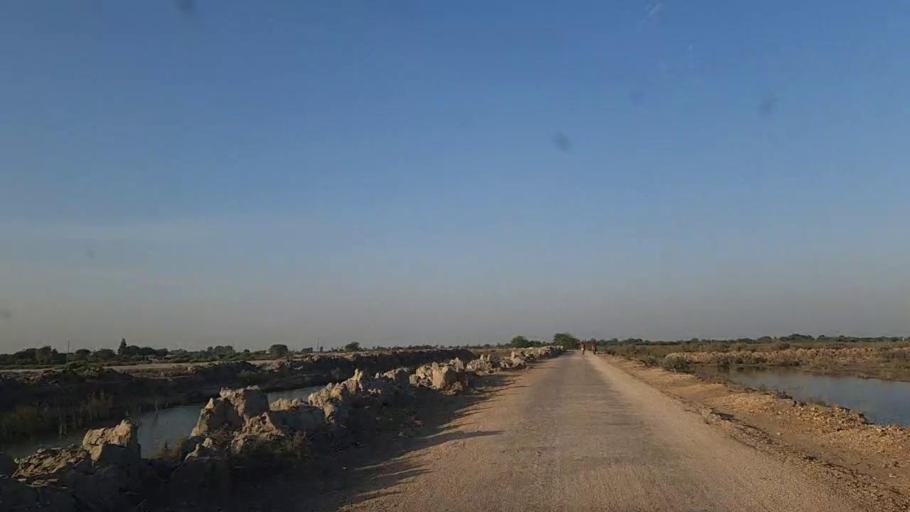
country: PK
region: Sindh
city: Mirpur Batoro
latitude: 24.6944
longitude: 68.2002
